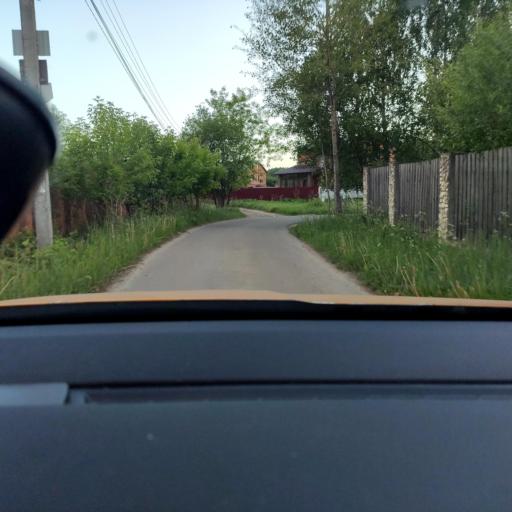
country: RU
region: Moskovskaya
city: Andreyevskoye
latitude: 55.5177
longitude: 37.9629
